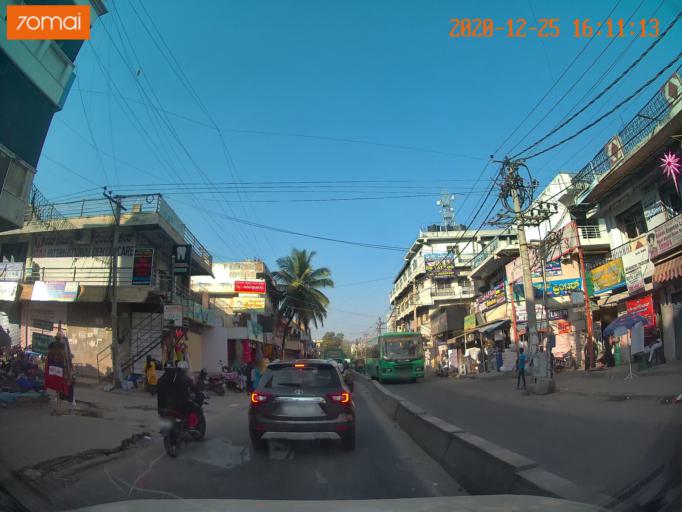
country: IN
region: Karnataka
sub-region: Bangalore Urban
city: Bangalore
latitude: 12.9042
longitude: 77.6274
